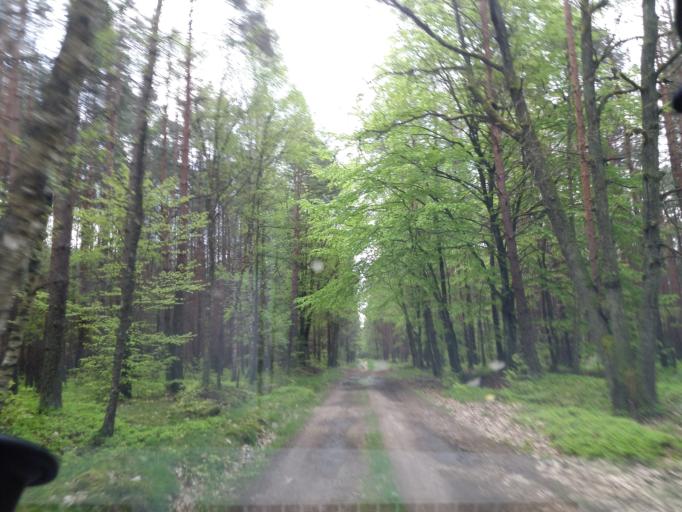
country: PL
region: West Pomeranian Voivodeship
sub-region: Powiat choszczenski
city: Drawno
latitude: 53.1132
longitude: 15.8679
